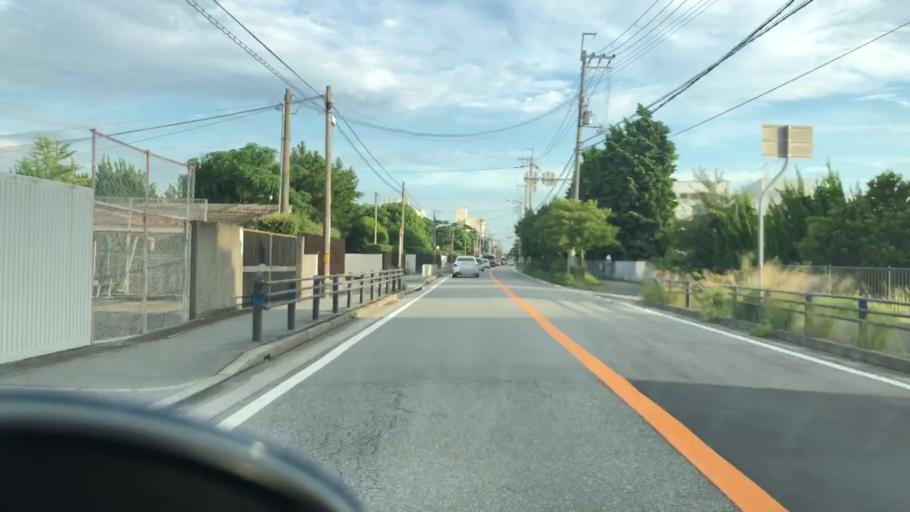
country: JP
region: Hyogo
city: Takarazuka
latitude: 34.7815
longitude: 135.3704
